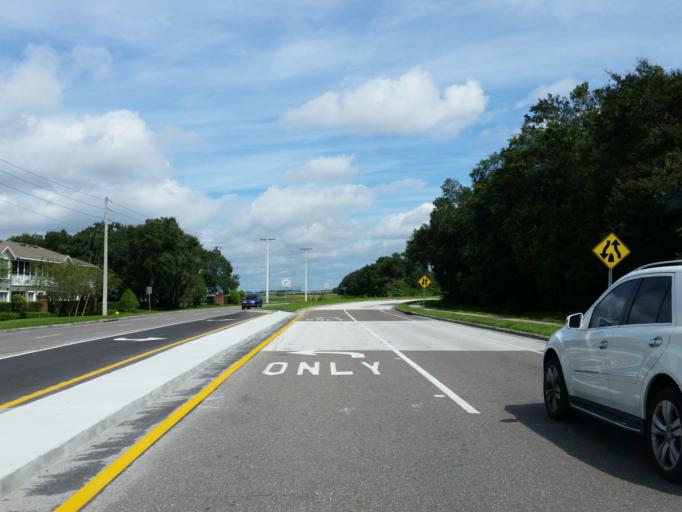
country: US
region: Florida
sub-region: Hillsborough County
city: Progress Village
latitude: 27.8999
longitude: -82.3311
